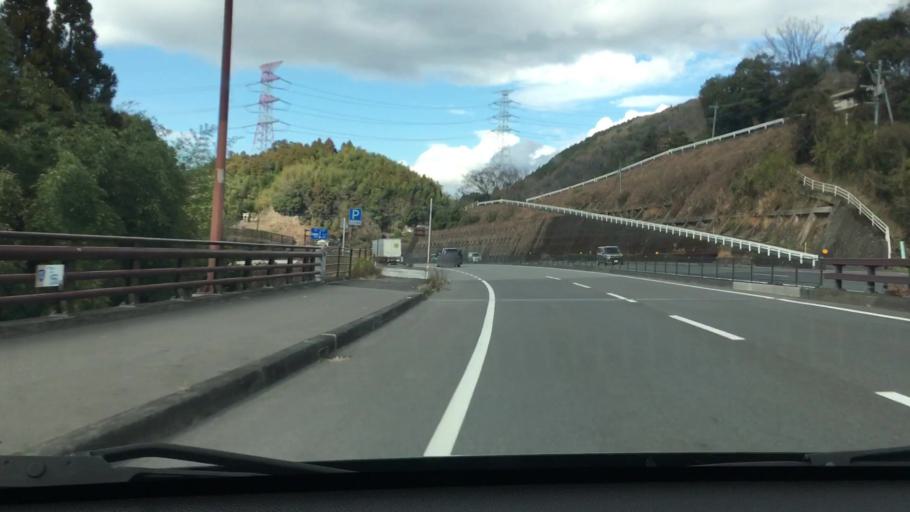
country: JP
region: Oita
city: Oita
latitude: 33.1104
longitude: 131.6567
